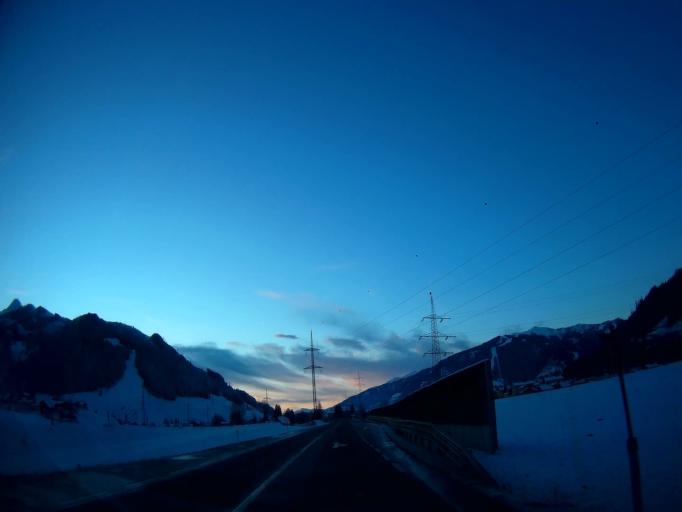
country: AT
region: Salzburg
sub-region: Politischer Bezirk Zell am See
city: Bruck an der Grossglocknerstrasse
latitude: 47.2793
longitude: 12.8384
